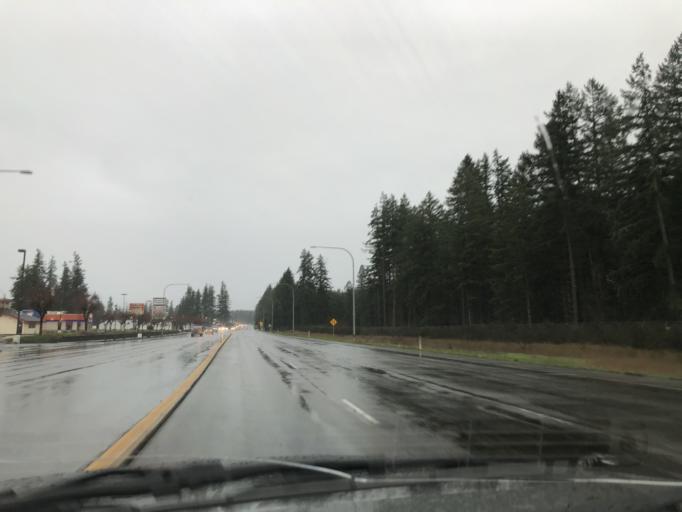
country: US
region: Washington
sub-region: Pierce County
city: Spanaway
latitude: 47.0964
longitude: -122.4352
